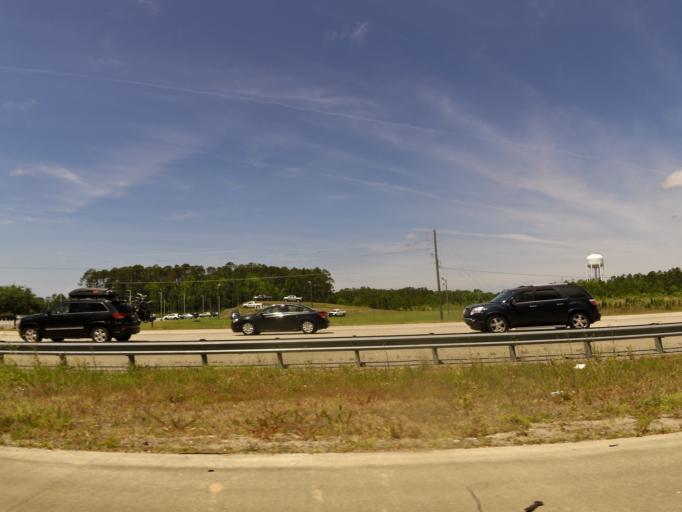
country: US
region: Georgia
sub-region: Glynn County
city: Country Club Estates
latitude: 31.2532
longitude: -81.4977
